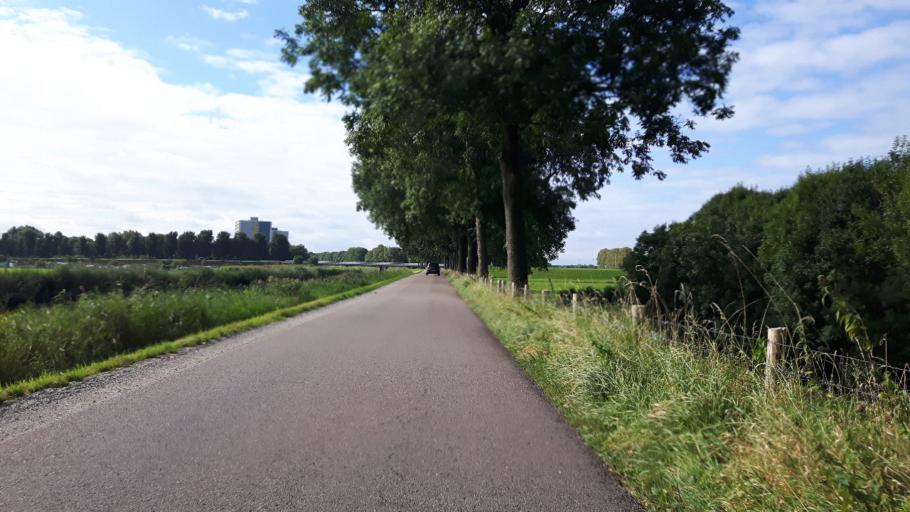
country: NL
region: North Holland
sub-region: Gemeente Purmerend
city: Purmerend
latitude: 52.5328
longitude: 4.9587
